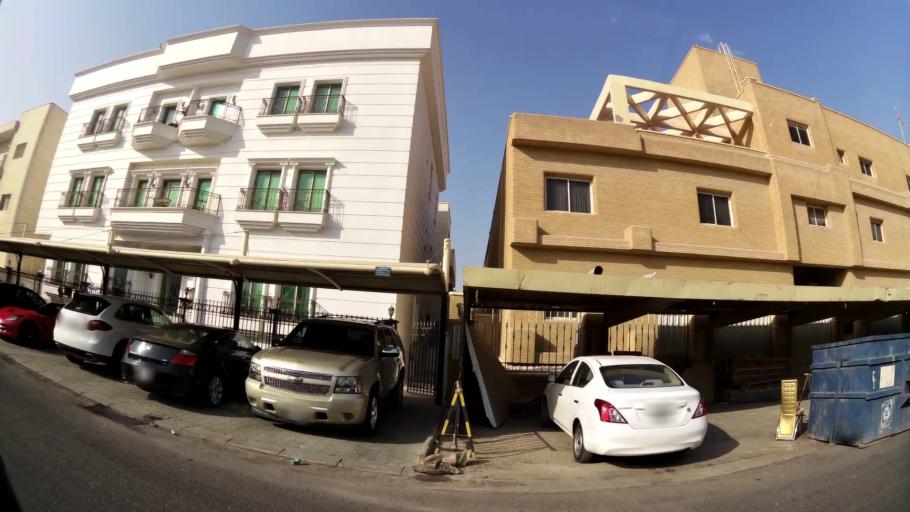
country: KW
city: Bayan
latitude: 29.3168
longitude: 48.0386
